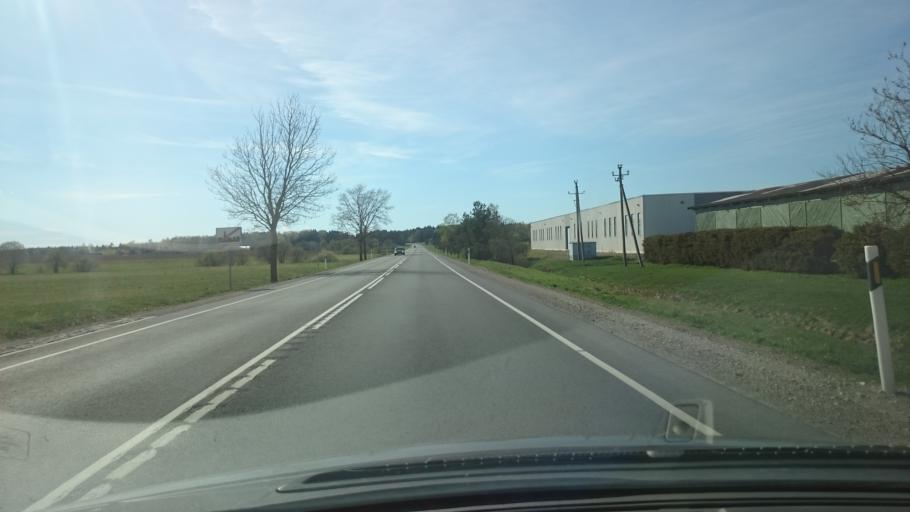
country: EE
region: Laeaene-Virumaa
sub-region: Kadrina vald
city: Kadrina
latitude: 59.3533
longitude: 26.2092
